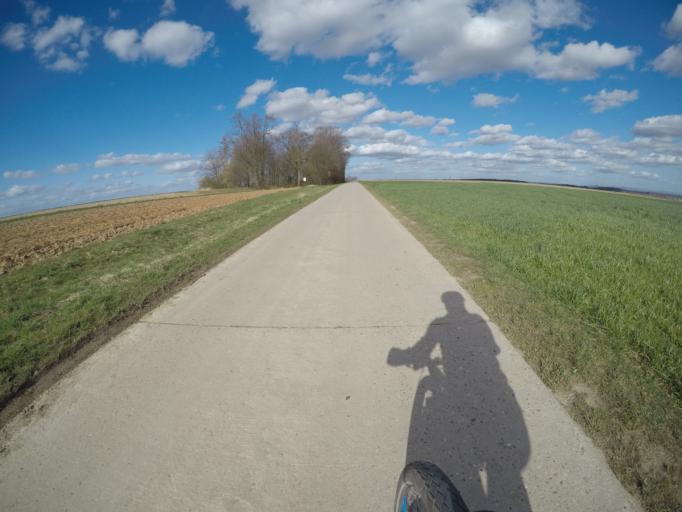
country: DE
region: Baden-Wuerttemberg
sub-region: Regierungsbezirk Stuttgart
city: Wolfschlugen
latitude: 48.6556
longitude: 9.2540
